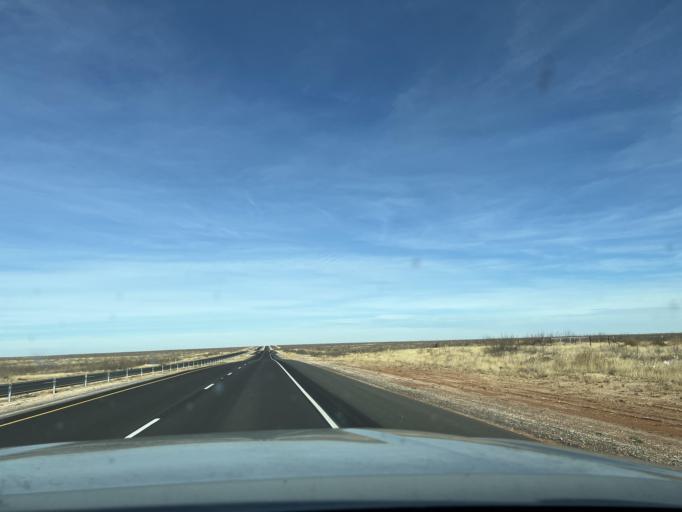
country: US
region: Texas
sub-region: Ector County
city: Gardendale
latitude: 32.0412
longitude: -102.4359
